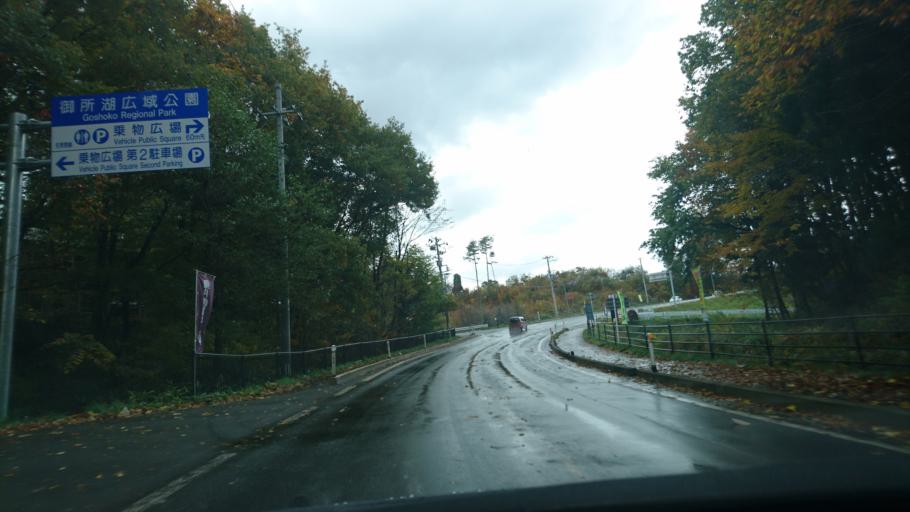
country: JP
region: Iwate
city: Shizukuishi
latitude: 39.6675
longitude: 140.9695
